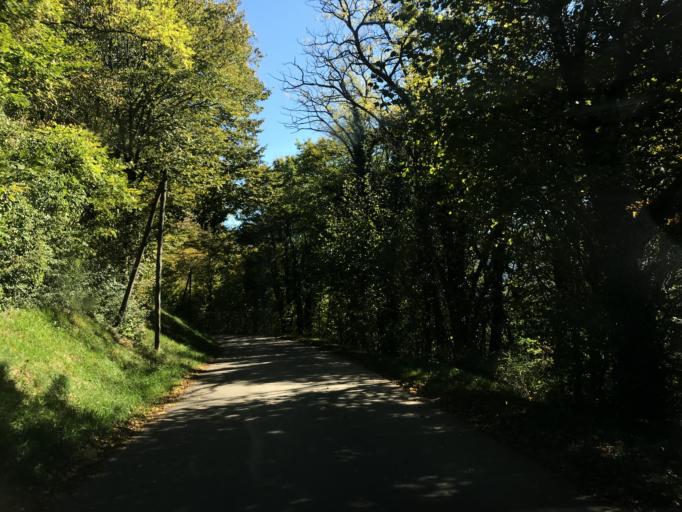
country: FR
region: Franche-Comte
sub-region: Departement du Doubs
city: Thise
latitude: 47.2841
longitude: 6.0867
